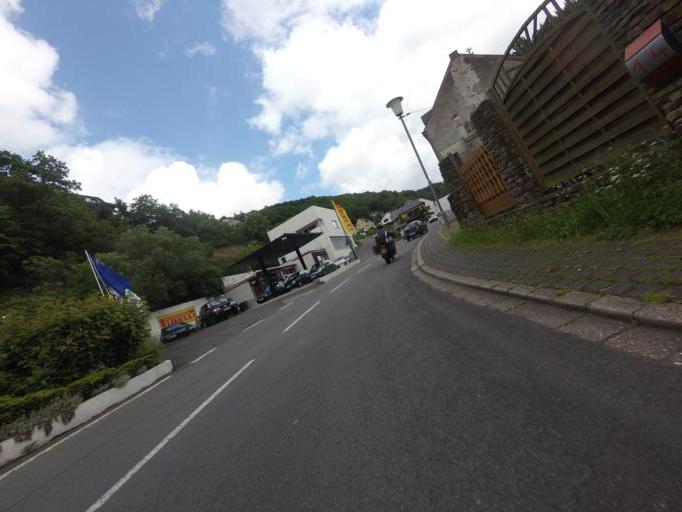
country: DE
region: Rheinland-Pfalz
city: Virneburg
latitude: 50.3425
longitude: 7.0809
